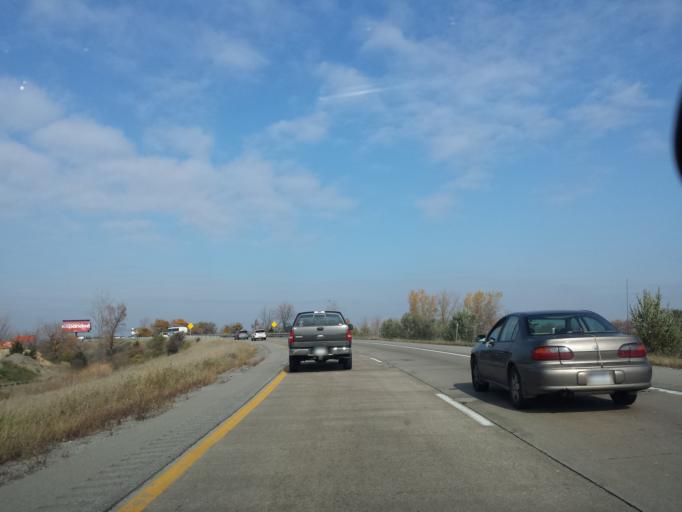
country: US
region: Michigan
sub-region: Saginaw County
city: Buena Vista
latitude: 43.4308
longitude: -83.8889
